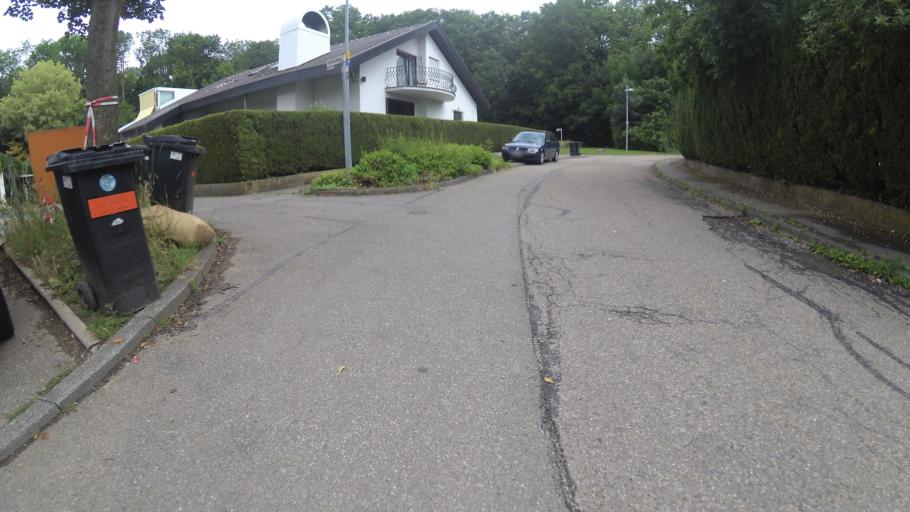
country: DE
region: Baden-Wuerttemberg
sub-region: Regierungsbezirk Stuttgart
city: Oedheim
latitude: 49.2151
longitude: 9.2476
